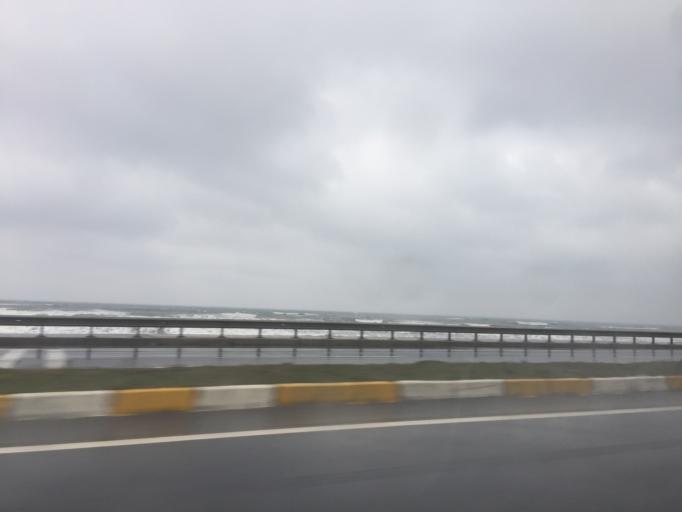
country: TR
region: Duzce
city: Akcakoca
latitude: 41.1042
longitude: 31.2525
